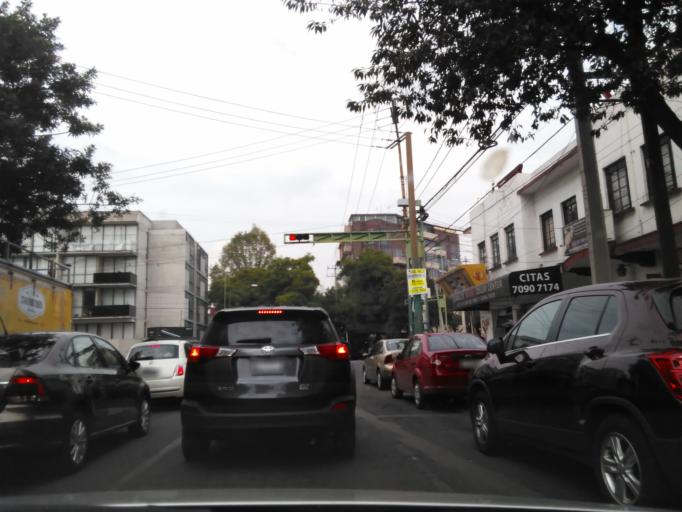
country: MX
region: Mexico City
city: Colonia del Valle
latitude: 19.3875
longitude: -99.1698
